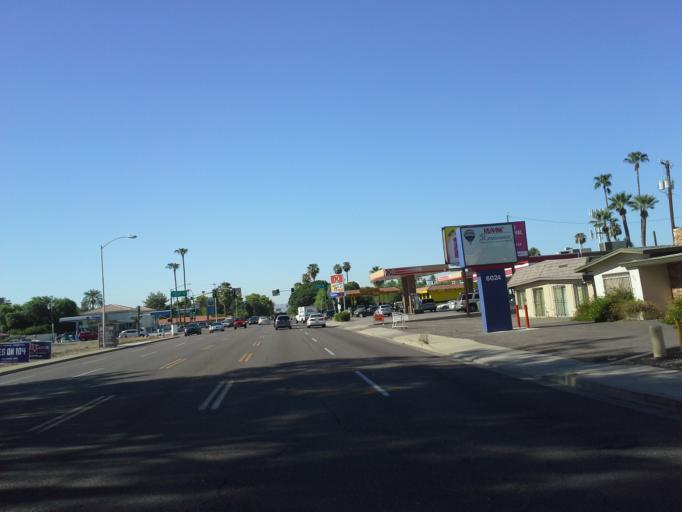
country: US
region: Arizona
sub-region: Maricopa County
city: Phoenix
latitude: 33.5251
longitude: -112.0825
